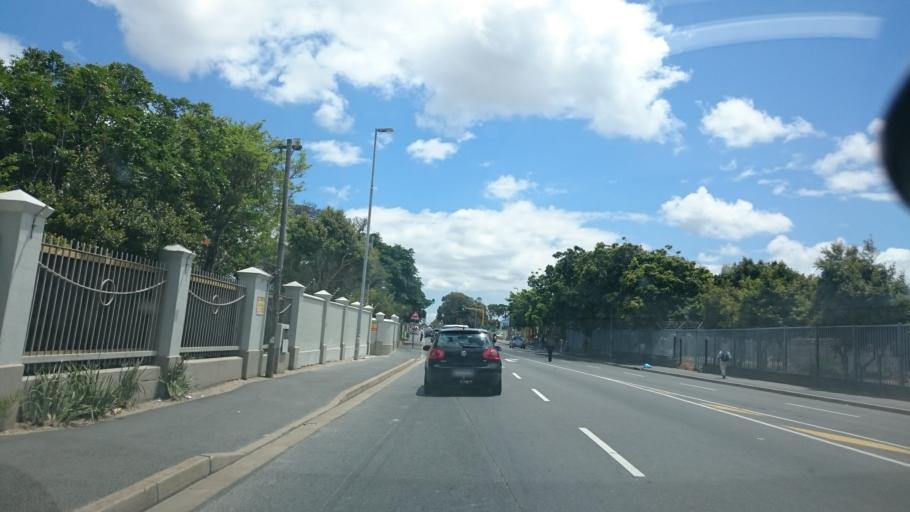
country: ZA
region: Western Cape
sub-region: City of Cape Town
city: Bergvliet
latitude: -34.0615
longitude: 18.4597
